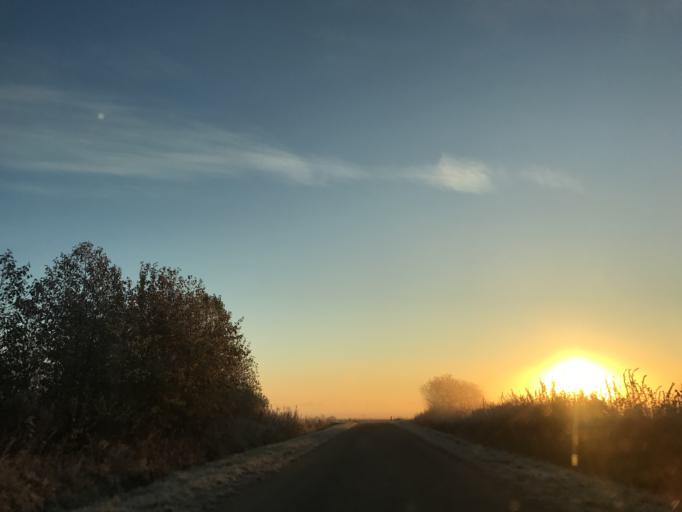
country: DK
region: South Denmark
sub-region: Haderslev Kommune
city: Haderslev
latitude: 55.2066
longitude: 9.4899
